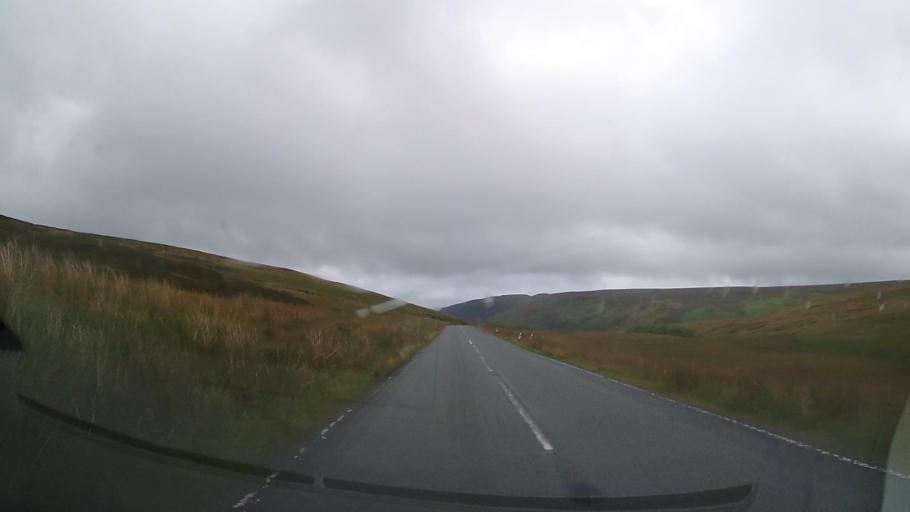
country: GB
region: Wales
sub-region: Denbighshire
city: Llandrillo
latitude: 52.8625
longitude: -3.4599
